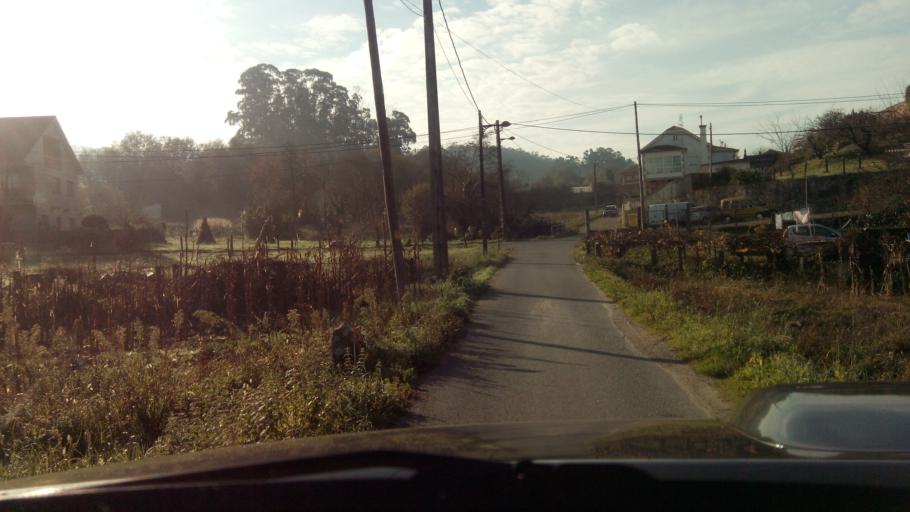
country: ES
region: Galicia
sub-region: Provincia de Pontevedra
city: Marin
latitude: 42.3631
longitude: -8.7365
